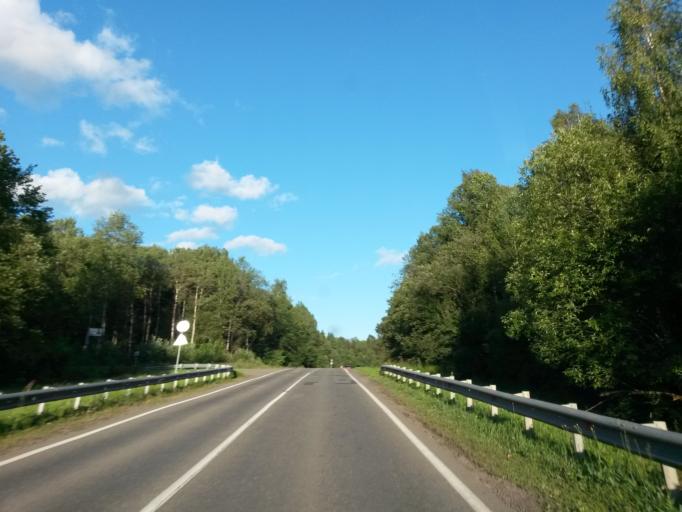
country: RU
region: Jaroslavl
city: Yaroslavl
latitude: 57.8019
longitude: 39.8213
